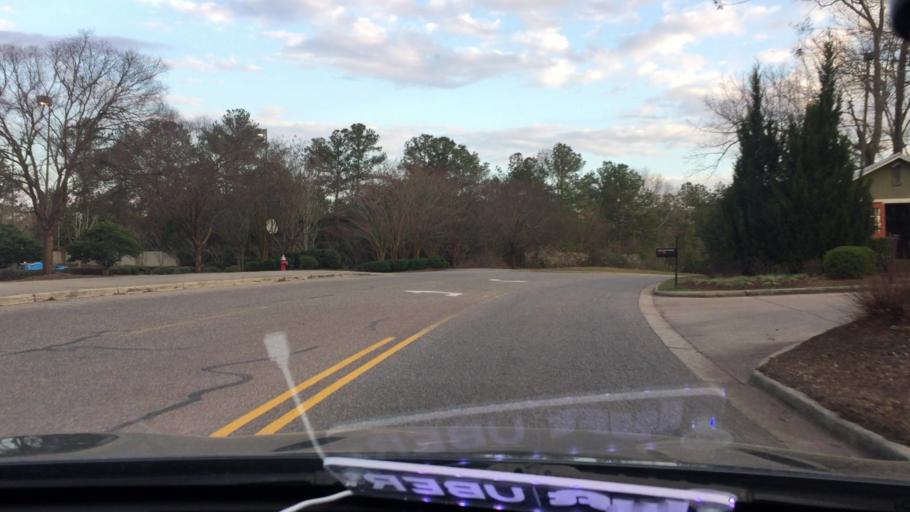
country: US
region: Alabama
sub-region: Lee County
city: Auburn
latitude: 32.5843
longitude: -85.4887
